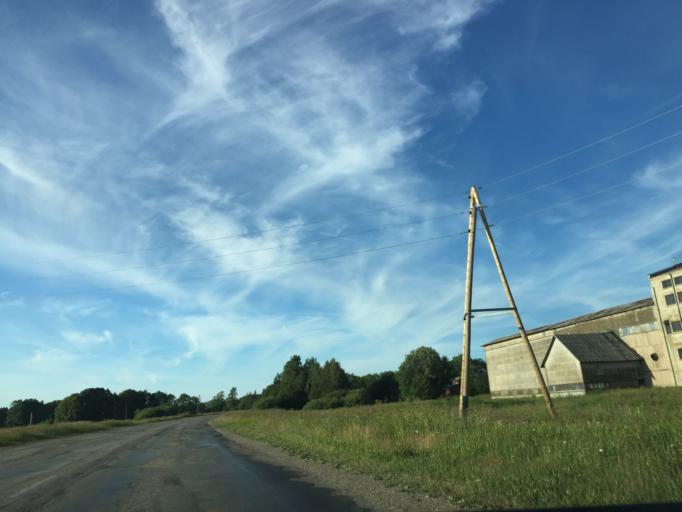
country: LV
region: Ventspils
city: Ventspils
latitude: 57.3132
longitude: 21.5565
